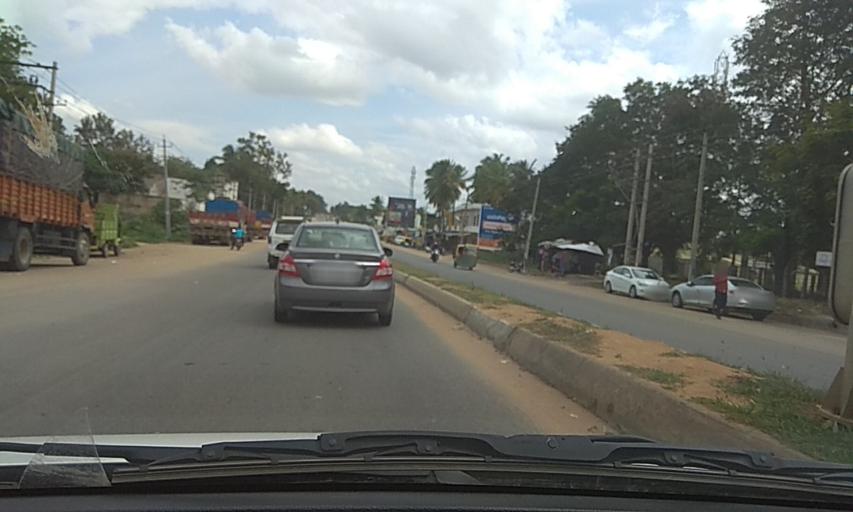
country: IN
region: Karnataka
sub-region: Tumkur
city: Tumkur
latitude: 13.3750
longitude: 77.0997
